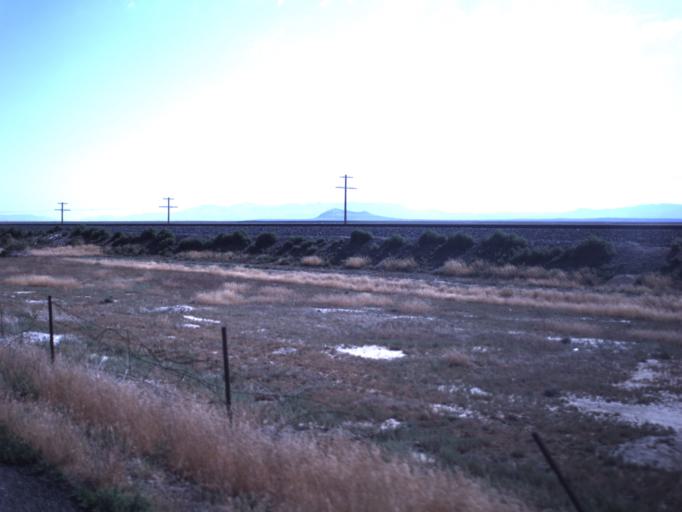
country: US
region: Utah
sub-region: Millard County
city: Delta
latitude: 38.9999
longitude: -112.7876
